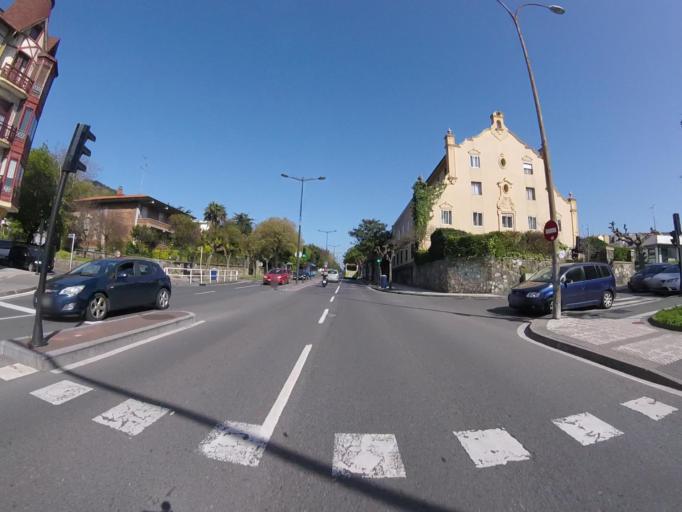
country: ES
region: Basque Country
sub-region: Provincia de Guipuzcoa
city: San Sebastian
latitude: 43.3217
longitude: -1.9599
